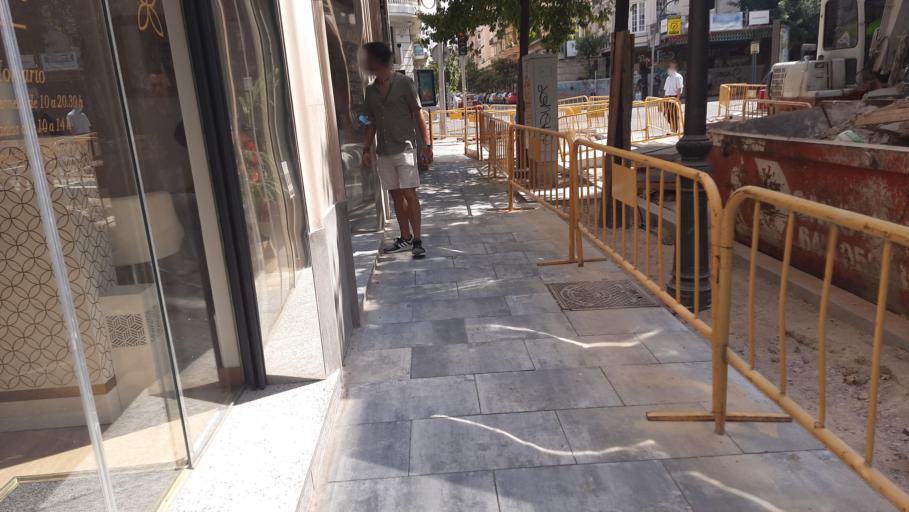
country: ES
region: Madrid
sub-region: Provincia de Madrid
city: Salamanca
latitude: 40.4236
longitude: -3.6763
